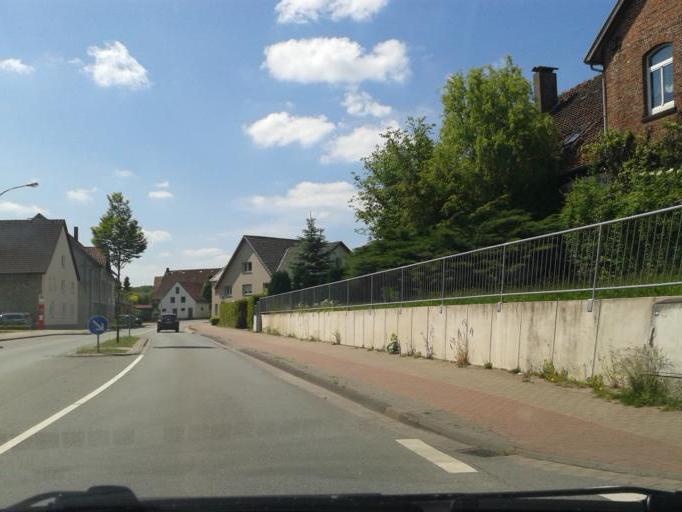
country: DE
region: North Rhine-Westphalia
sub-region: Regierungsbezirk Detmold
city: Steinheim
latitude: 51.8971
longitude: 9.0565
